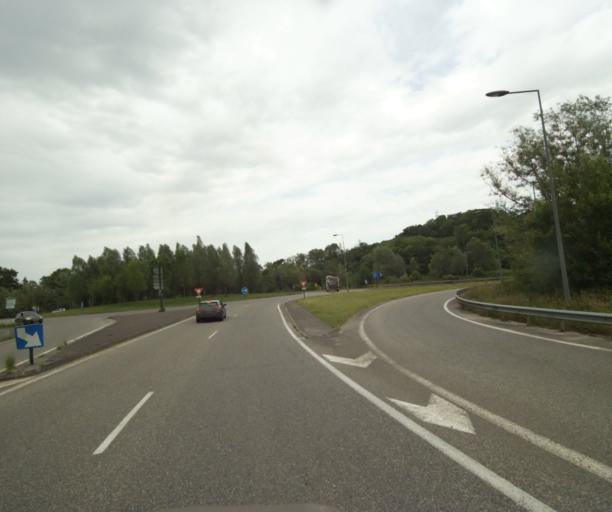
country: FR
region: Aquitaine
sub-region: Departement des Pyrenees-Atlantiques
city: Mouguerre
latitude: 43.4797
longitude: -1.4417
